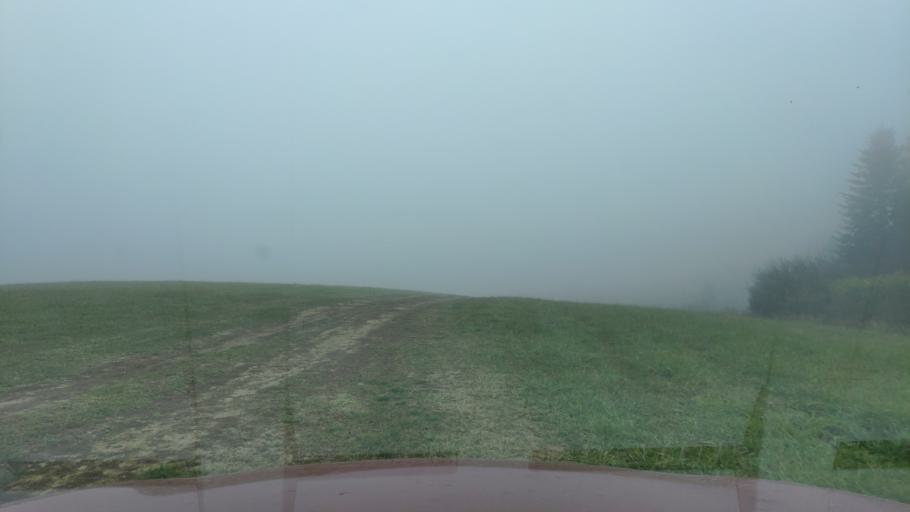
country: SK
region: Presovsky
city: Sabinov
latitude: 49.1396
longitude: 21.2278
